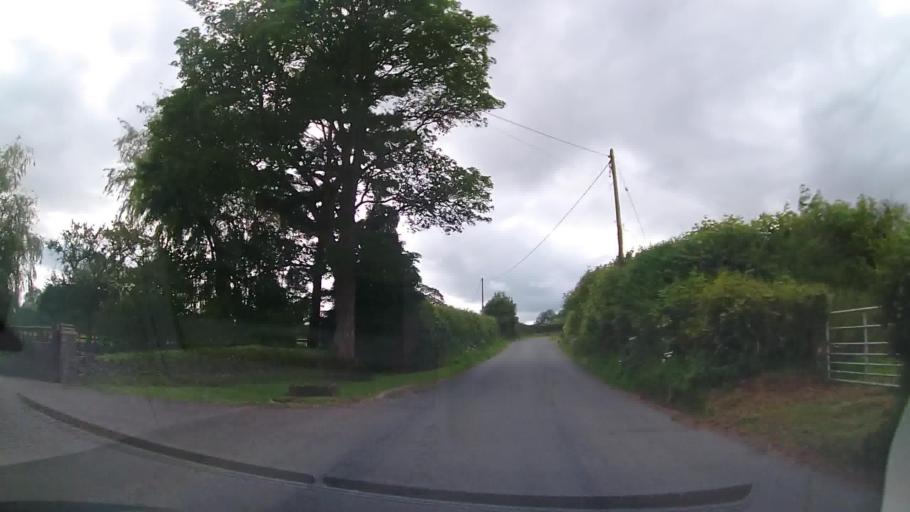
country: GB
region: England
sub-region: Shropshire
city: Wem
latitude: 52.9029
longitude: -2.7160
